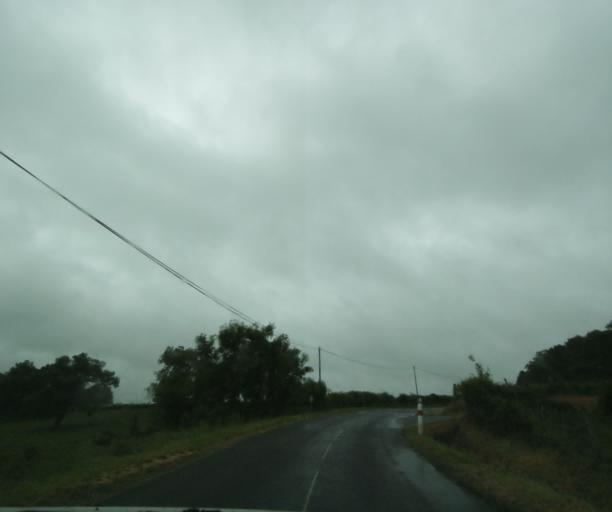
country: FR
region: Bourgogne
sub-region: Departement de Saone-et-Loire
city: Palinges
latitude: 46.5401
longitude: 4.2144
